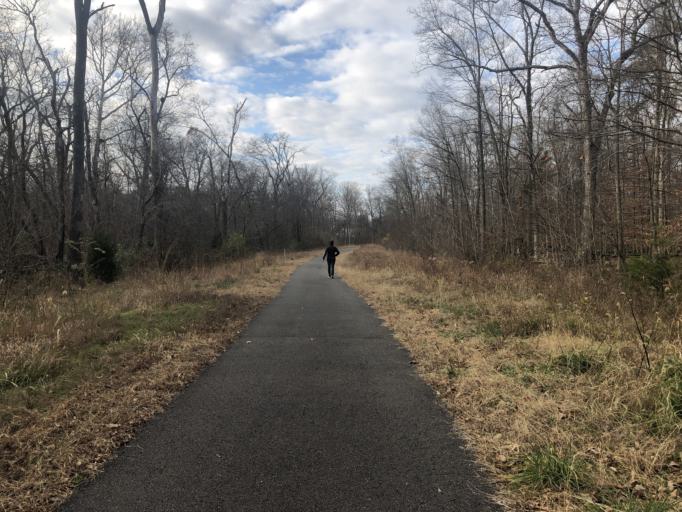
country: US
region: Virginia
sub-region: Fairfax County
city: Centreville
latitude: 38.8485
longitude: -77.4742
